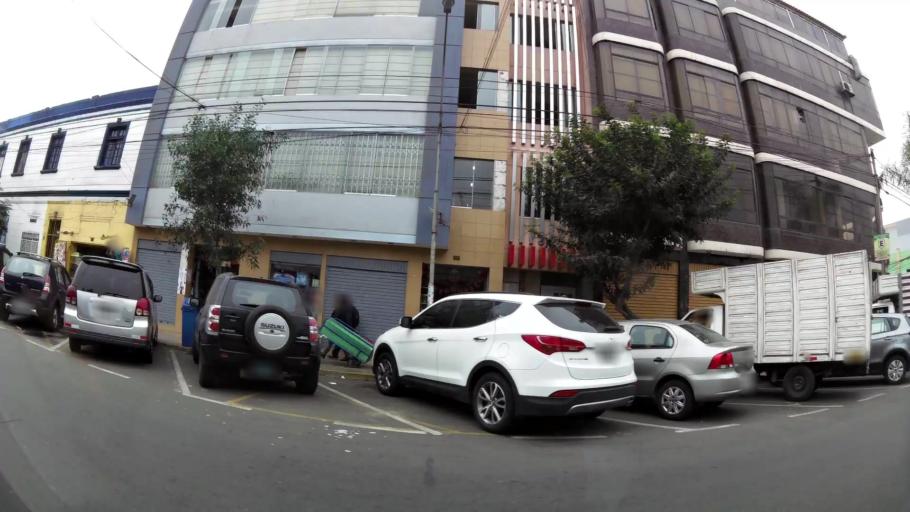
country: PE
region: Lima
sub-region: Lima
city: San Isidro
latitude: -12.0858
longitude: -77.0325
